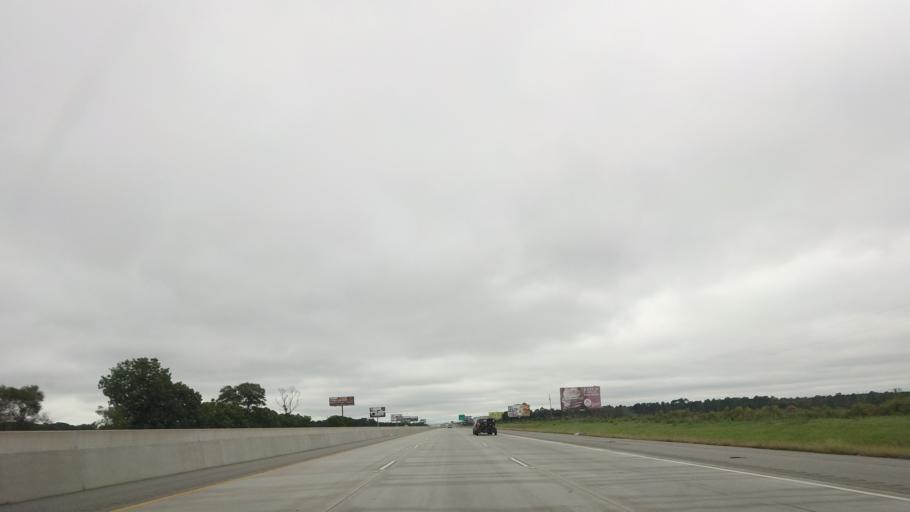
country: US
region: Georgia
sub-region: Cook County
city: Sparks
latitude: 31.1801
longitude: -83.4527
